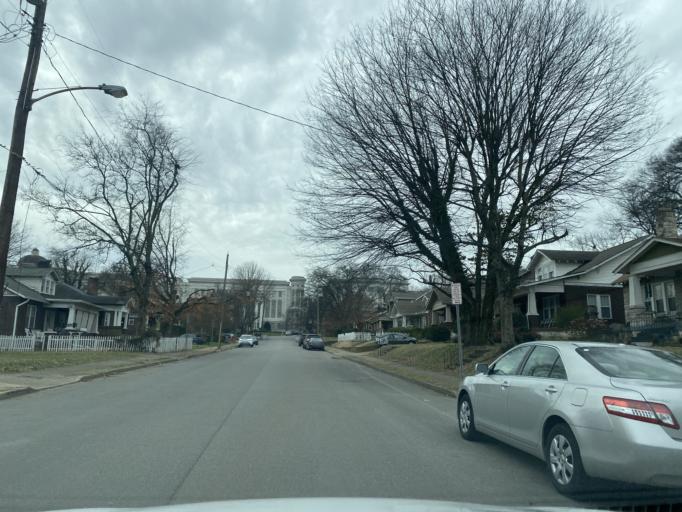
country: US
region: Tennessee
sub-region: Davidson County
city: Nashville
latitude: 36.1378
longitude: -86.7930
